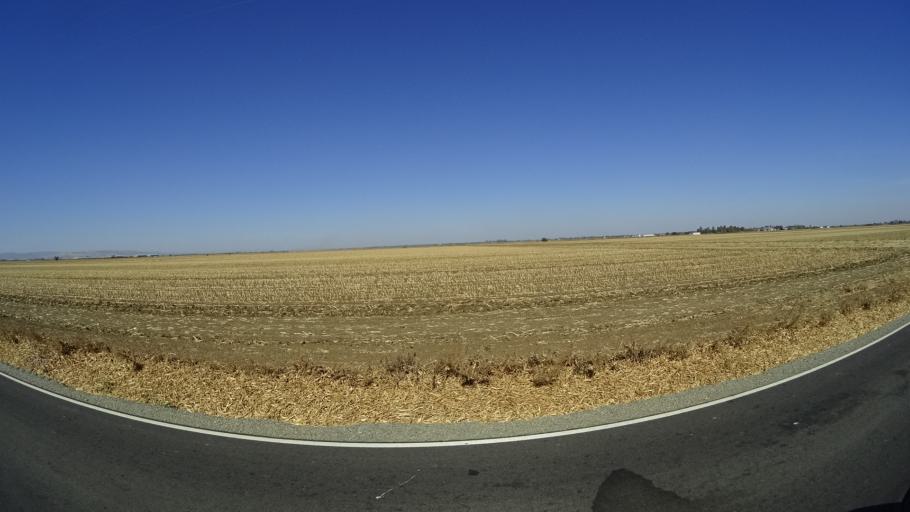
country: US
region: California
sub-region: Yolo County
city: Cottonwood
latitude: 38.6198
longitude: -121.9051
